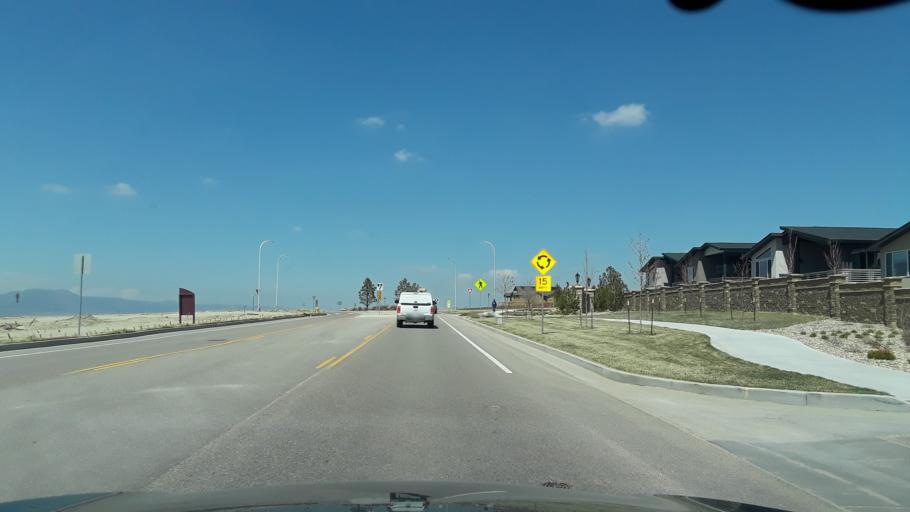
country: US
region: Colorado
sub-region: El Paso County
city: Black Forest
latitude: 38.9825
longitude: -104.7572
